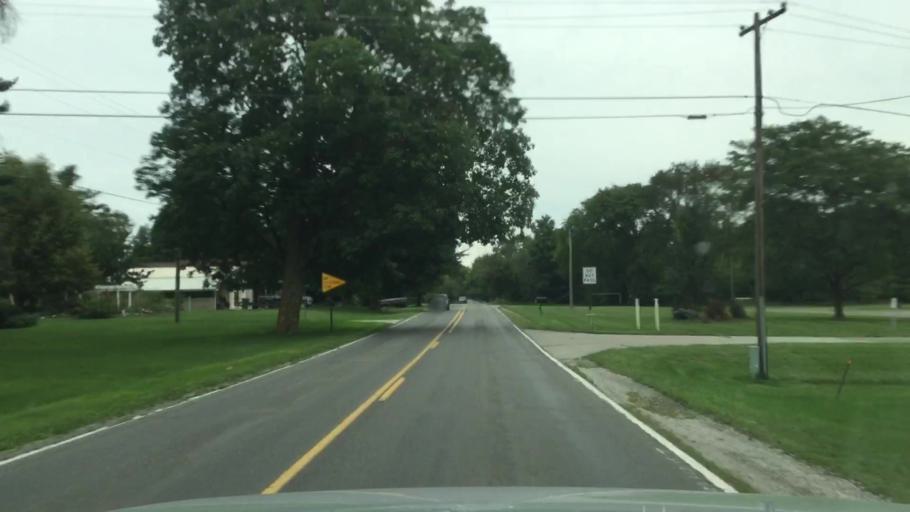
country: US
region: Michigan
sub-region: Washtenaw County
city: Milan
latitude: 42.1614
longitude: -83.6506
